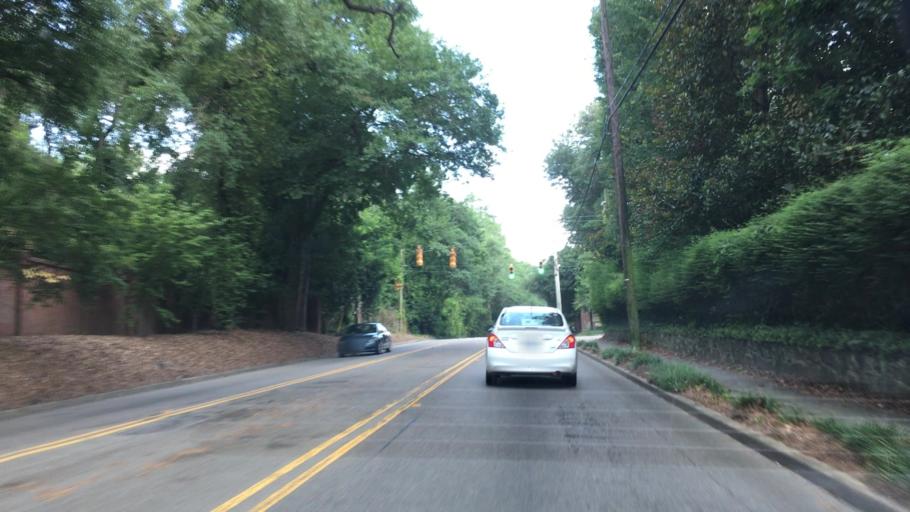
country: US
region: South Carolina
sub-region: Aiken County
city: Aiken
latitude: 33.5495
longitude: -81.7219
